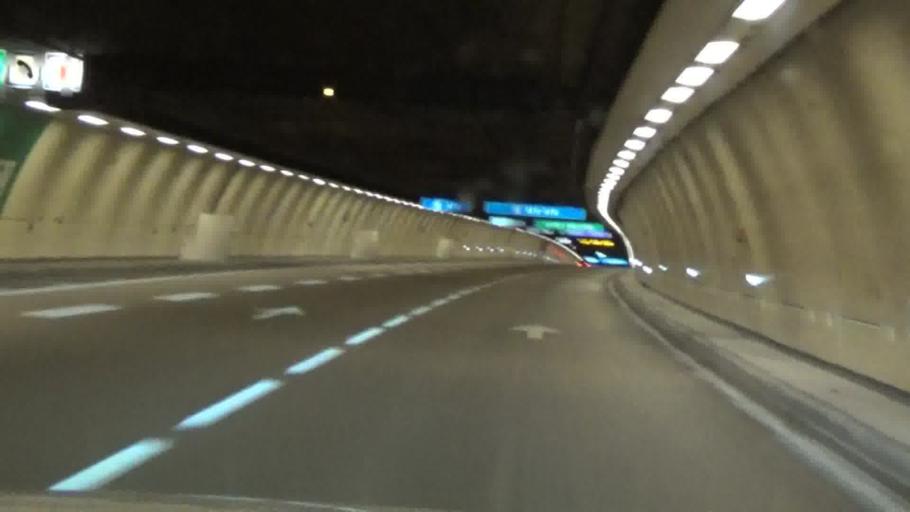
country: FR
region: Ile-de-France
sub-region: Departement des Hauts-de-Seine
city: Vaucresson
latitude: 48.8267
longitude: 2.1497
